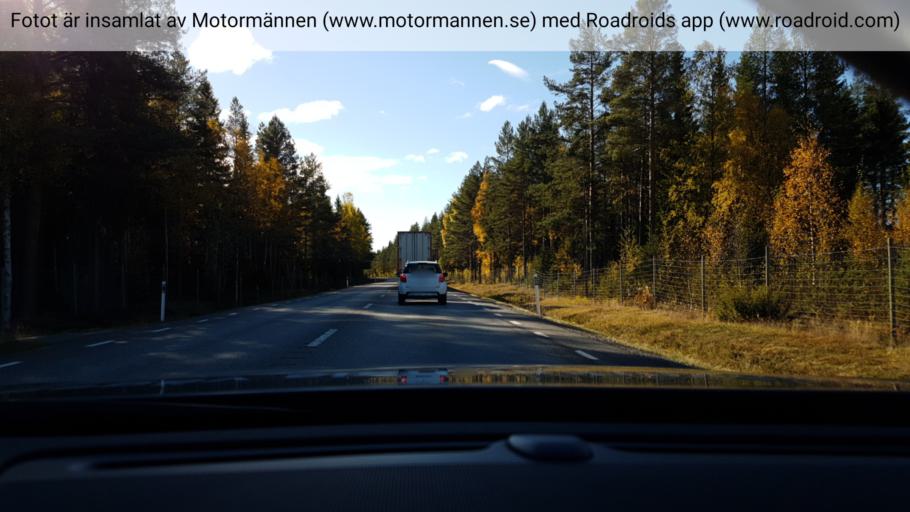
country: SE
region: Vaesterbotten
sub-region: Skelleftea Kommun
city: Burea
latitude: 64.5308
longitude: 21.2582
